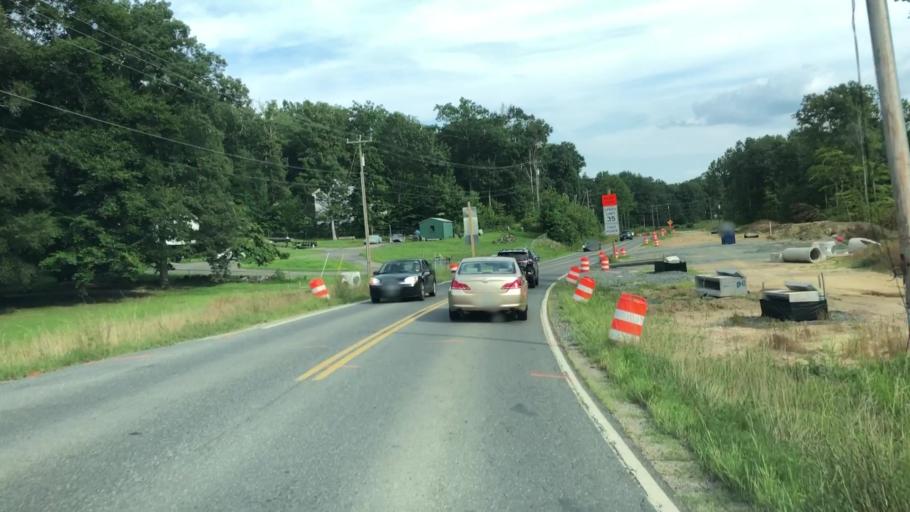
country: US
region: Virginia
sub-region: Stafford County
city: Stafford
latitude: 38.4318
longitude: -77.4397
